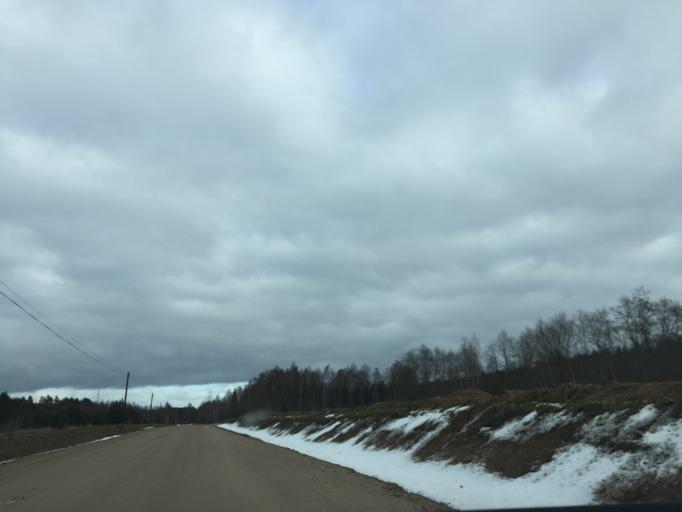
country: LV
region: Salacgrivas
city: Ainazi
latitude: 57.8531
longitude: 24.4913
